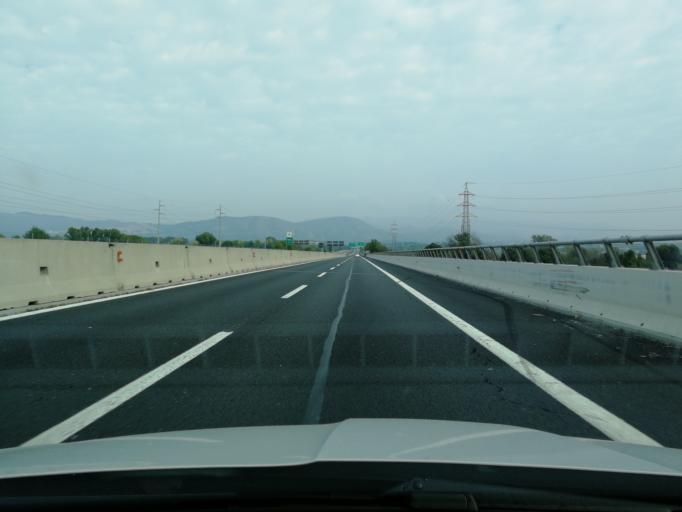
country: IT
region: Latium
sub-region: Citta metropolitana di Roma Capitale
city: Bagni di Tivoli
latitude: 41.9265
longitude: 12.7153
